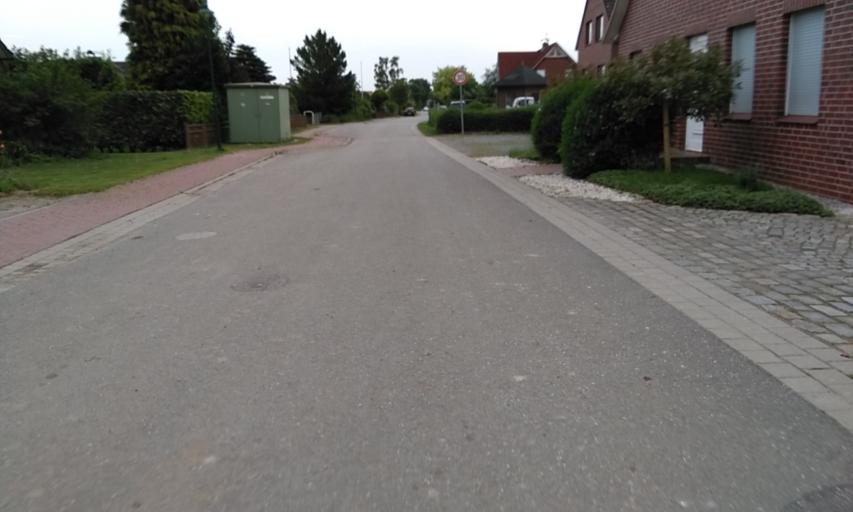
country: DE
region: Lower Saxony
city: Jork
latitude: 53.5133
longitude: 9.6919
